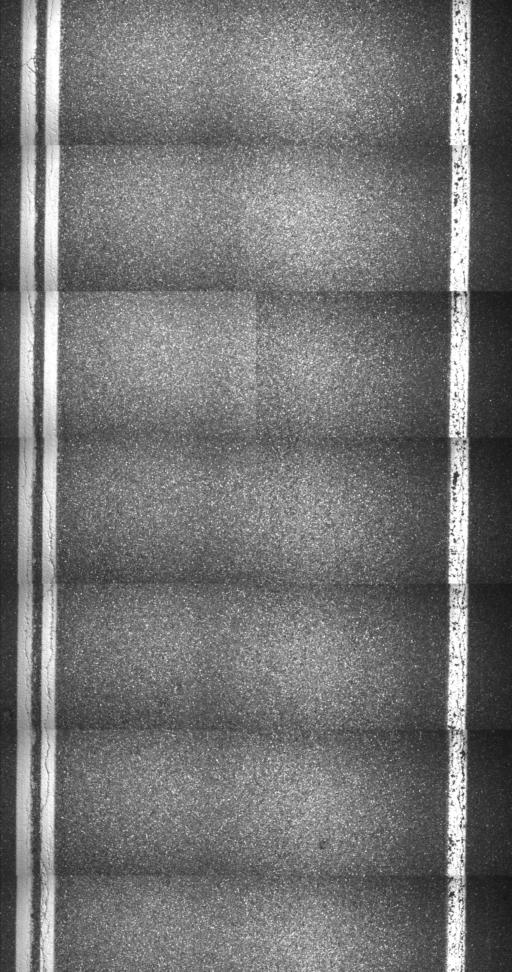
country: US
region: Massachusetts
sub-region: Berkshire County
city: North Adams
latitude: 42.8031
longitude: -72.9739
